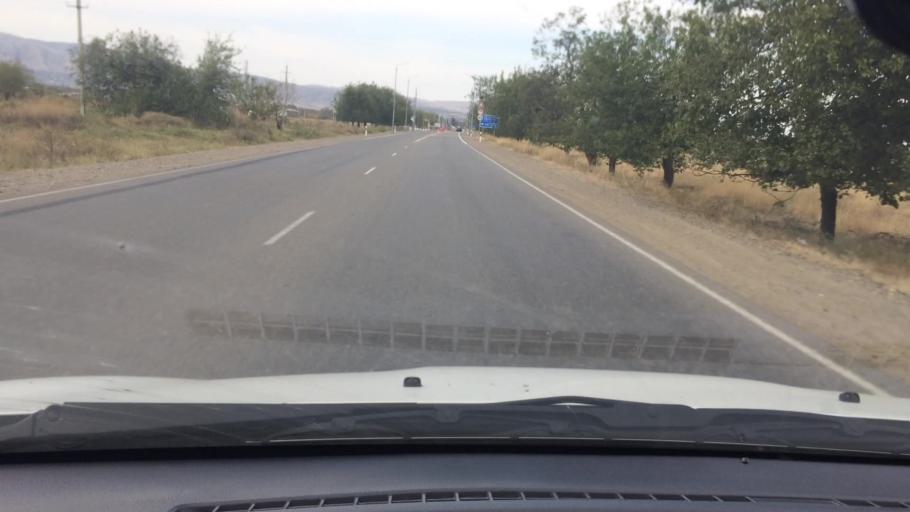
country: GE
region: Kvemo Kartli
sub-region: Marneuli
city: Marneuli
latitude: 41.5684
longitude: 44.7753
